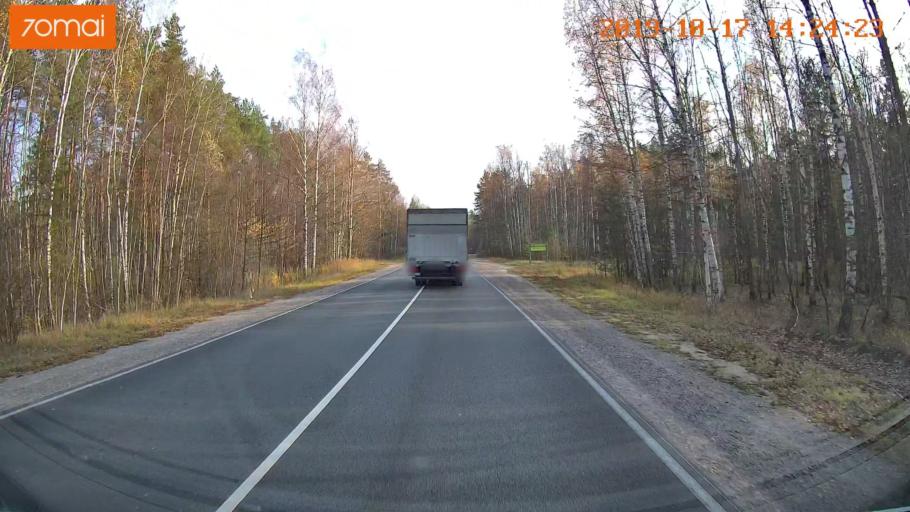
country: RU
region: Moskovskaya
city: Radovitskiy
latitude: 55.0097
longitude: 39.9675
